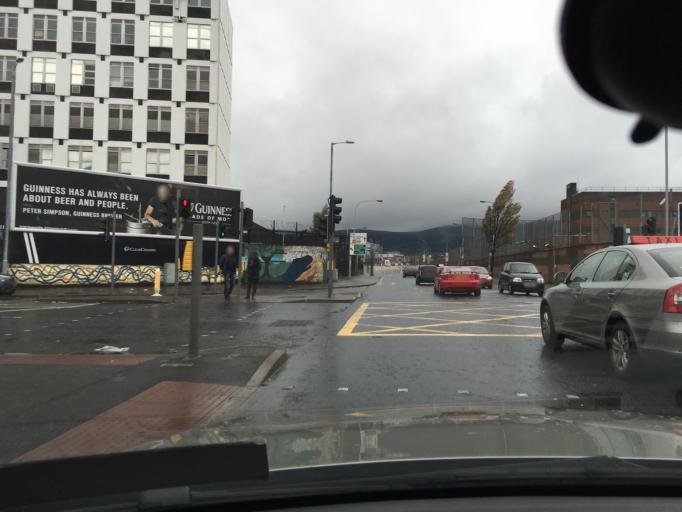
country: GB
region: Northern Ireland
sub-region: City of Belfast
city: Belfast
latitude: 54.5957
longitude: -5.9374
